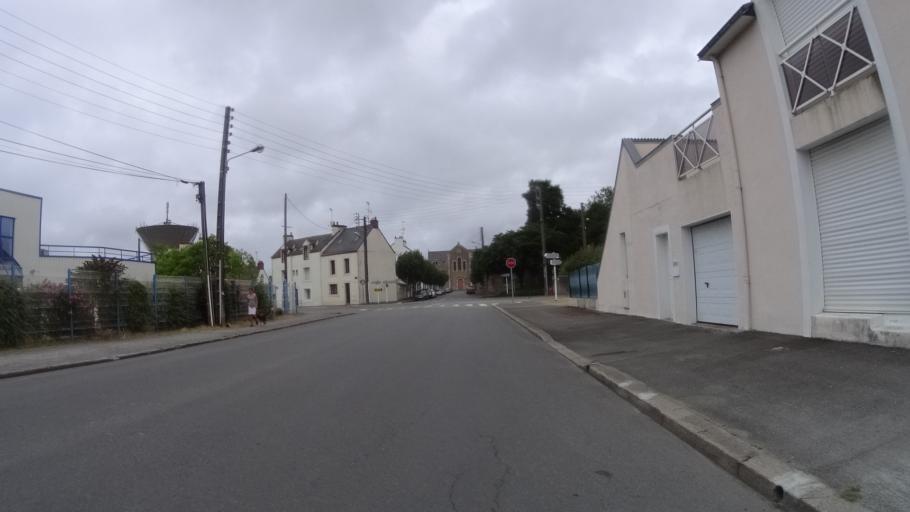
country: FR
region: Pays de la Loire
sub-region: Departement de la Loire-Atlantique
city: Trignac
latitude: 47.2984
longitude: -2.1849
